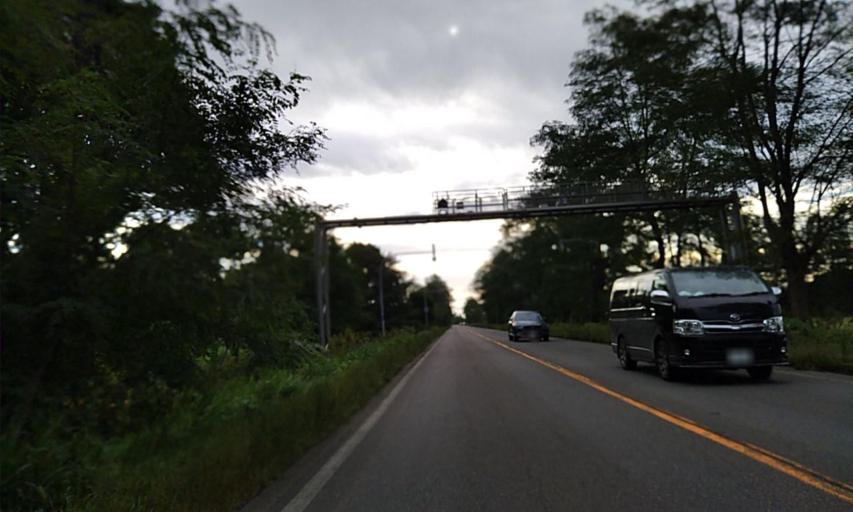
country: JP
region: Hokkaido
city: Obihiro
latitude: 42.9349
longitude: 142.9683
